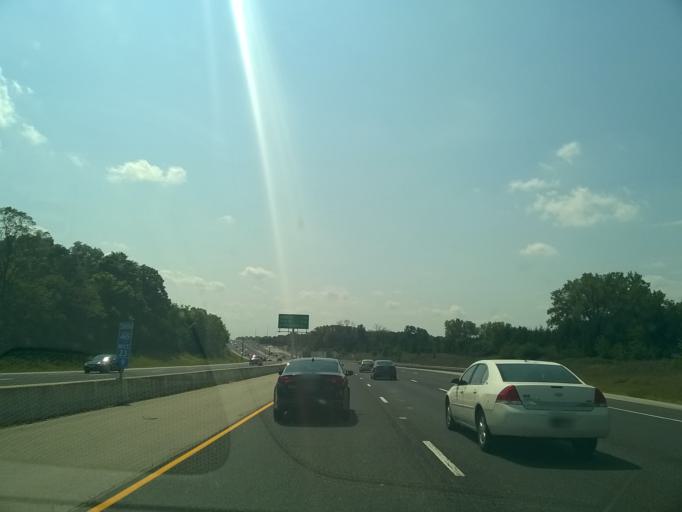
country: US
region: Indiana
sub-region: Boone County
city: Zionsville
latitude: 39.9214
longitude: -86.2696
